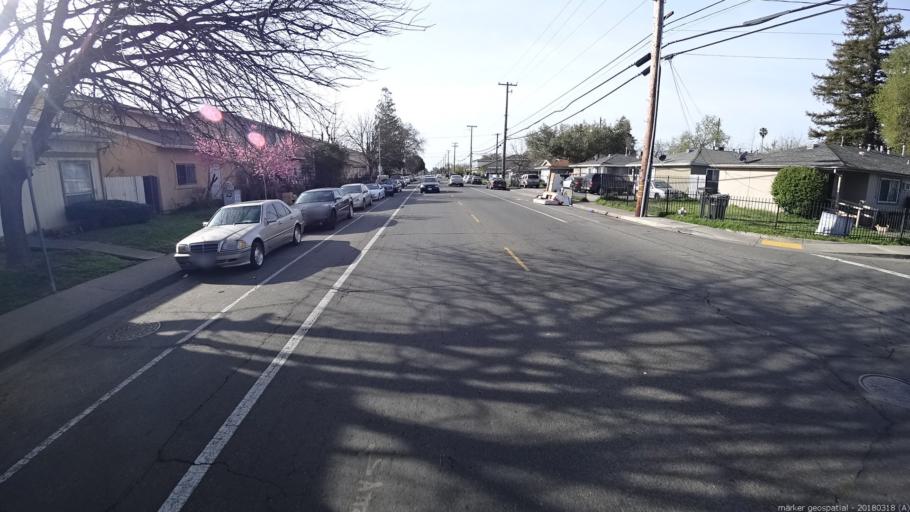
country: US
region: California
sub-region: Sacramento County
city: Parkway
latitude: 38.5385
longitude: -121.4647
